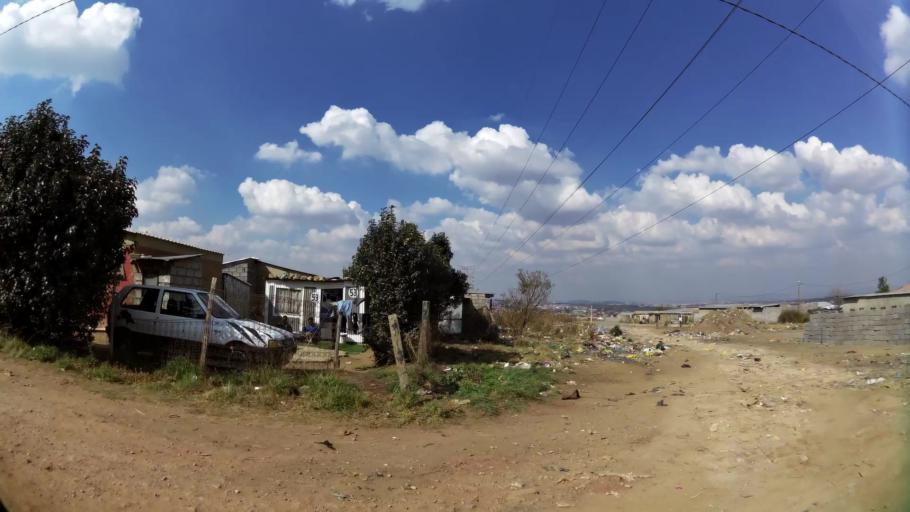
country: ZA
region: Gauteng
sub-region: City of Johannesburg Metropolitan Municipality
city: Roodepoort
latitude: -26.1958
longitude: 27.8706
